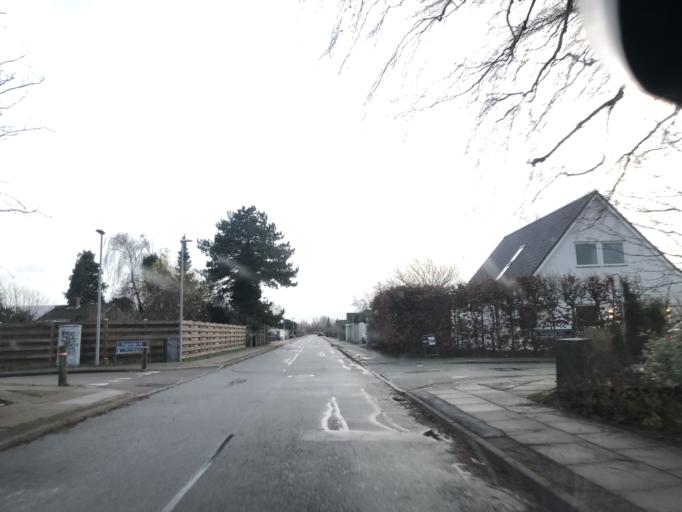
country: DK
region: Capital Region
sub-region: Tarnby Kommune
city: Tarnby
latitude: 55.6152
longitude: 12.6046
